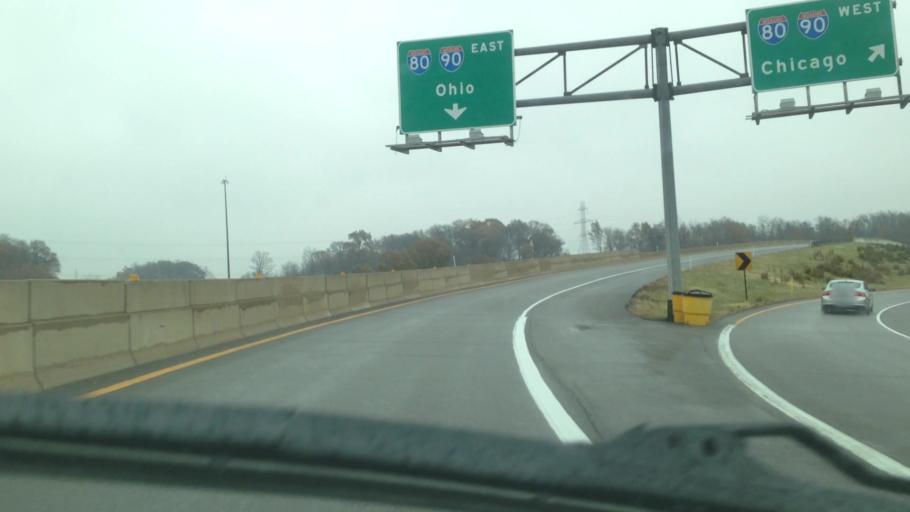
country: US
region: Indiana
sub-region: Saint Joseph County
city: Granger
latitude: 41.7332
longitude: -86.1432
